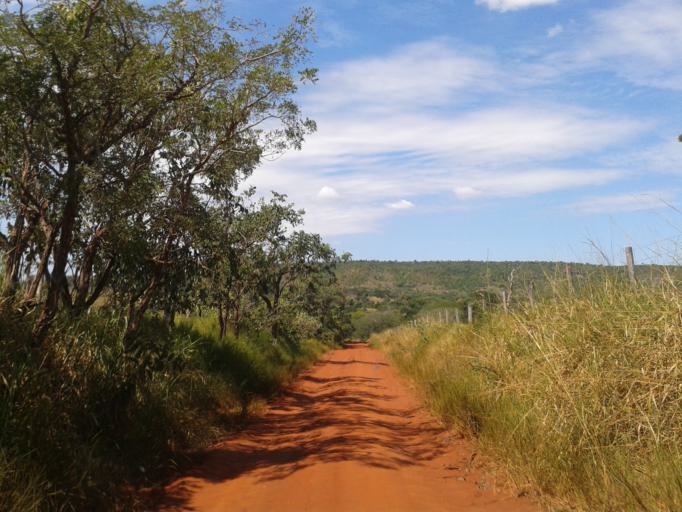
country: BR
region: Minas Gerais
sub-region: Campina Verde
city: Campina Verde
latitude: -19.4003
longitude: -49.7725
